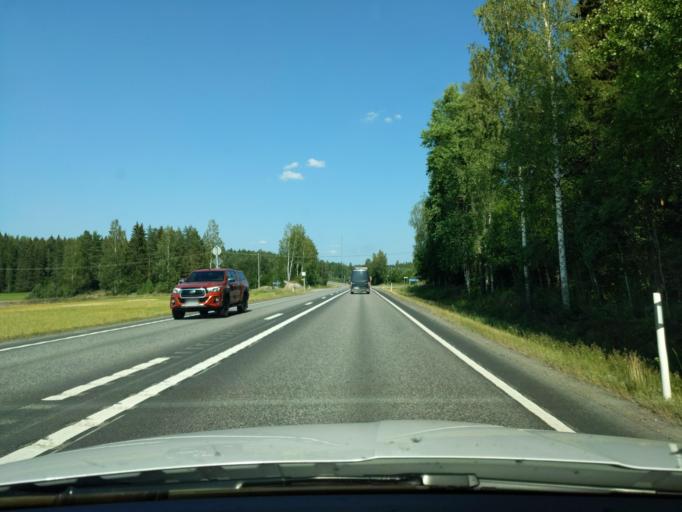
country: FI
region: Paijanne Tavastia
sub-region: Lahti
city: Jaervelae
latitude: 60.9097
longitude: 25.3371
